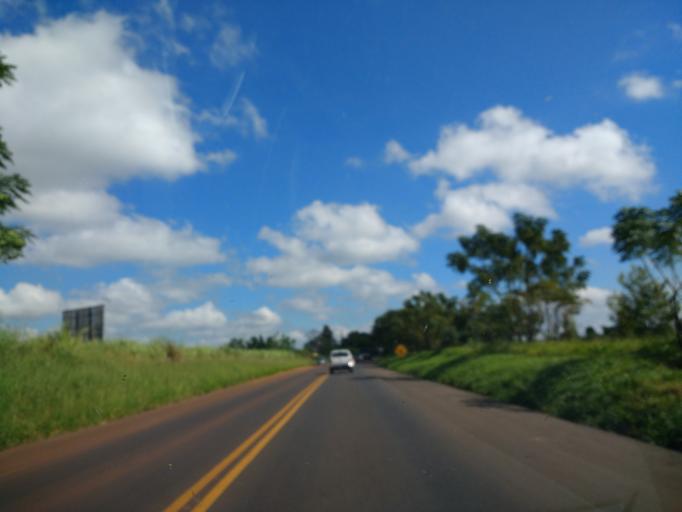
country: BR
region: Parana
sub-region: Umuarama
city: Umuarama
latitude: -23.8227
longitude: -53.3373
